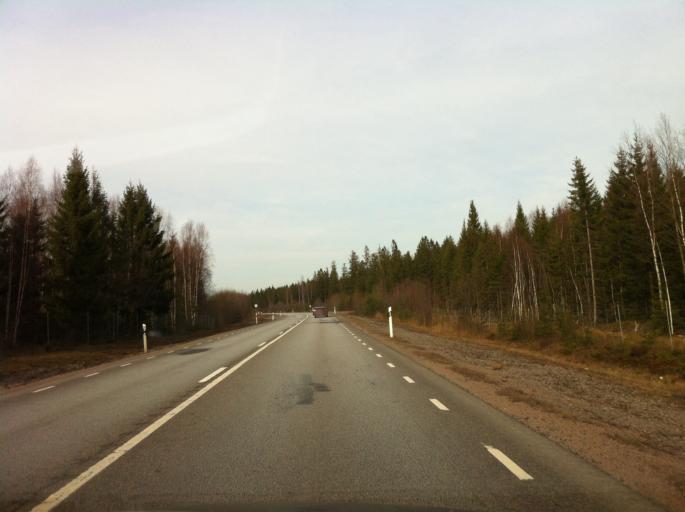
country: SE
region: Vaestra Goetaland
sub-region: Gullspangs Kommun
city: Gullspang
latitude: 58.8676
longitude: 14.0084
